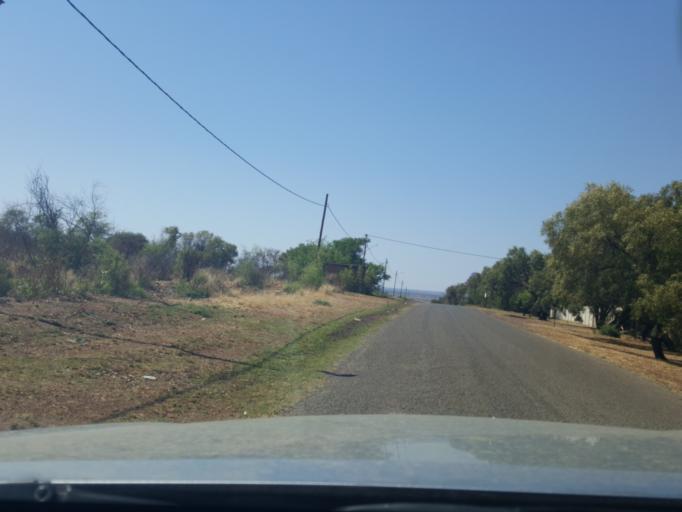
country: ZA
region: North-West
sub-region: Ngaka Modiri Molema District Municipality
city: Zeerust
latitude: -25.5303
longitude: 26.0811
